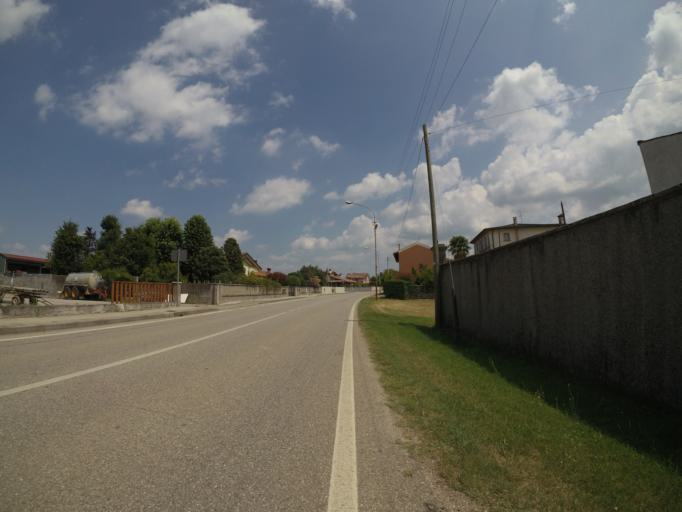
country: IT
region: Friuli Venezia Giulia
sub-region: Provincia di Udine
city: Mereto di Tomba
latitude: 46.0236
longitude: 13.0394
